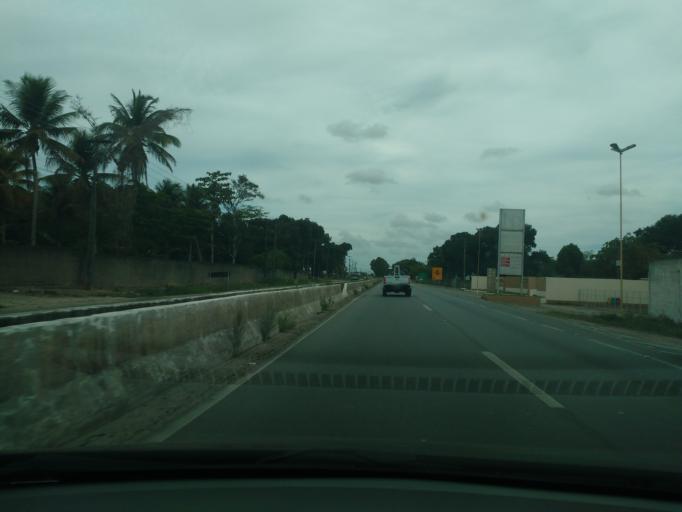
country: BR
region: Alagoas
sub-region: Rio Largo
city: Rio Largo
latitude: -9.4825
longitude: -35.8187
